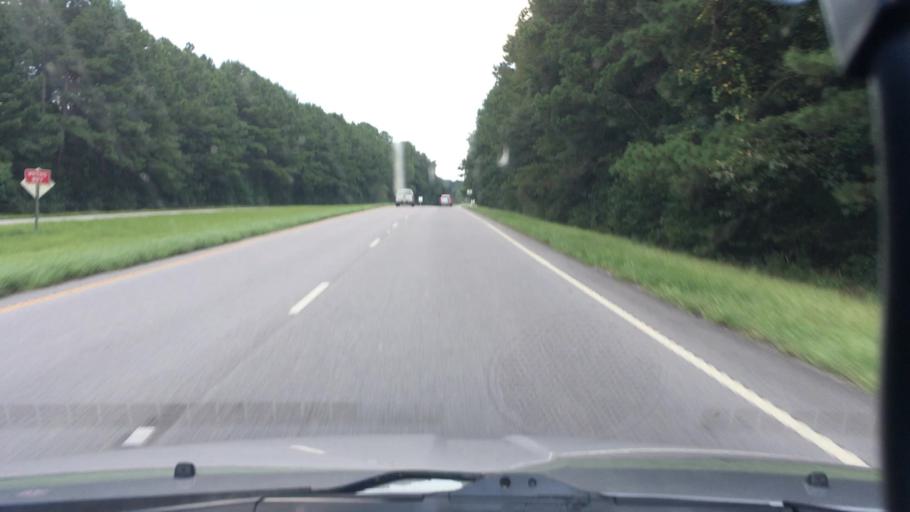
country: US
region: South Carolina
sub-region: Hampton County
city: Yemassee
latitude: 32.6285
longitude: -80.8316
